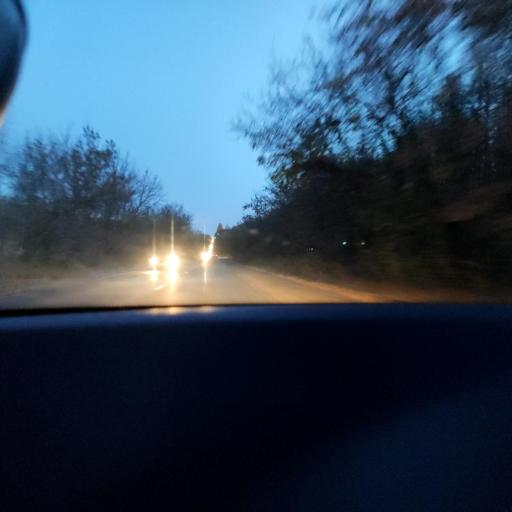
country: RU
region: Samara
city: Petra-Dubrava
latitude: 53.3133
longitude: 50.2730
